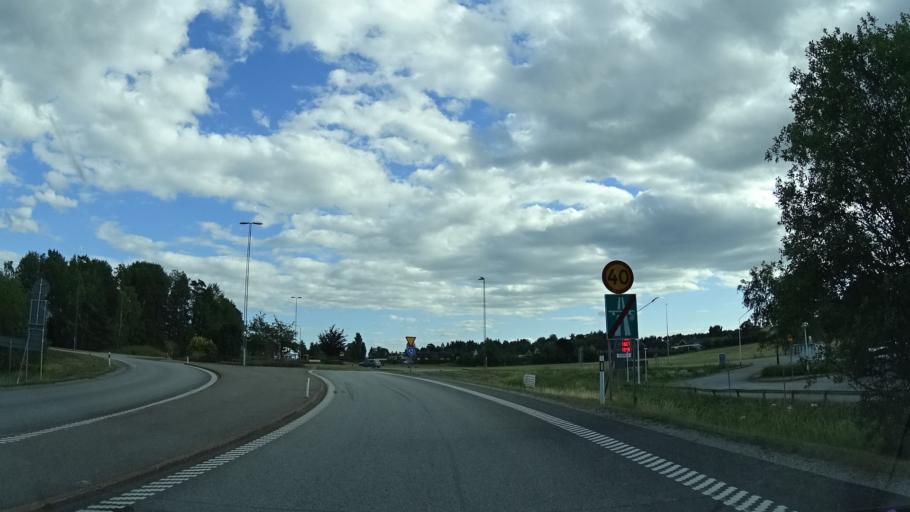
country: SE
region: Uppsala
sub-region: Habo Kommun
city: Balsta
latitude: 59.5851
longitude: 17.5059
